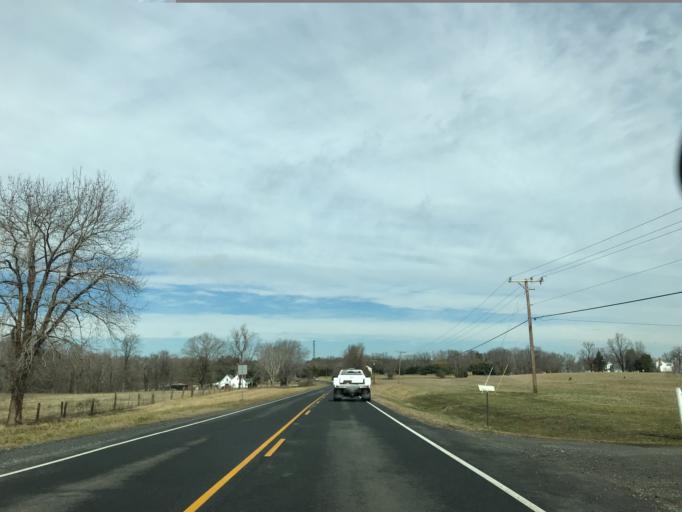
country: US
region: Virginia
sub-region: King George County
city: Dahlgren
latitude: 38.3284
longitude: -77.0824
